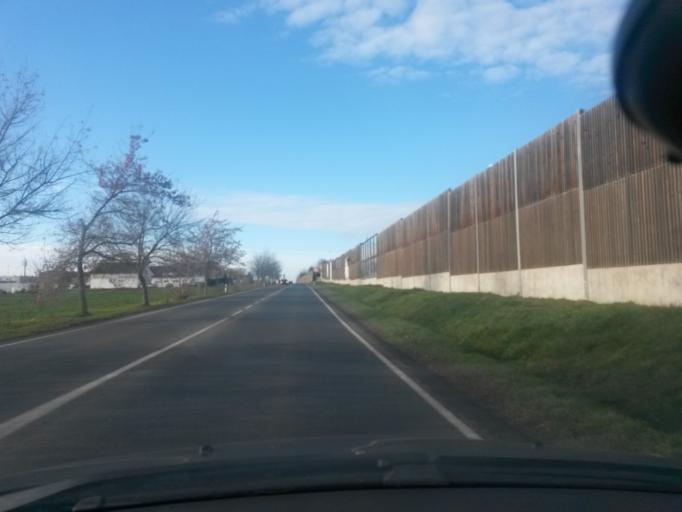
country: CZ
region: Central Bohemia
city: Jesenice
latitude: 49.9689
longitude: 14.5253
